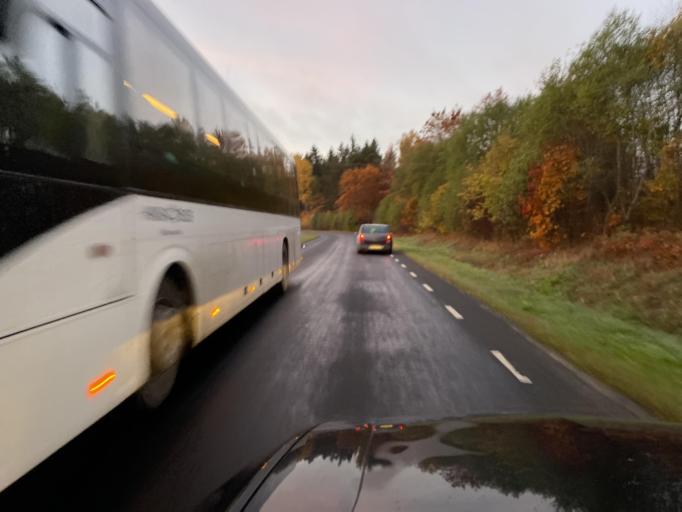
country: EE
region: Harju
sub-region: Nissi vald
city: Riisipere
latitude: 59.2384
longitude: 24.2440
